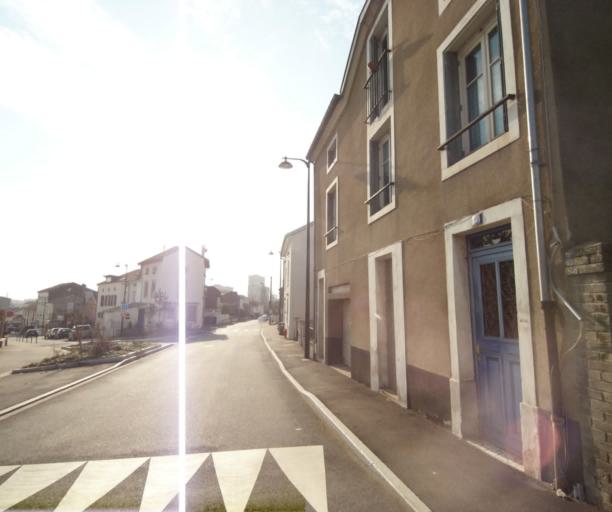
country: FR
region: Lorraine
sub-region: Departement de Meurthe-et-Moselle
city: Laxou
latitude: 48.6837
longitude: 6.1430
